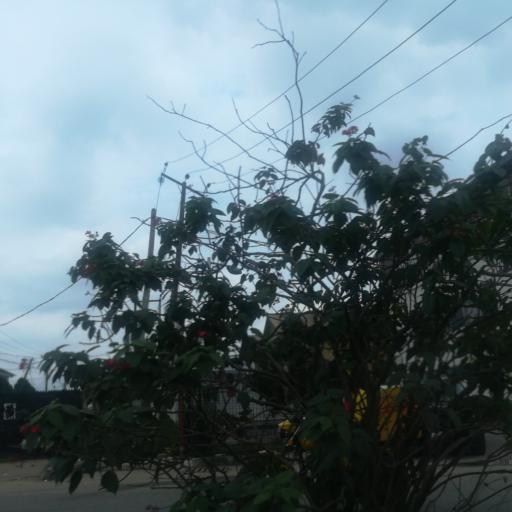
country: NG
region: Lagos
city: Ojota
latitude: 6.5764
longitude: 3.3897
